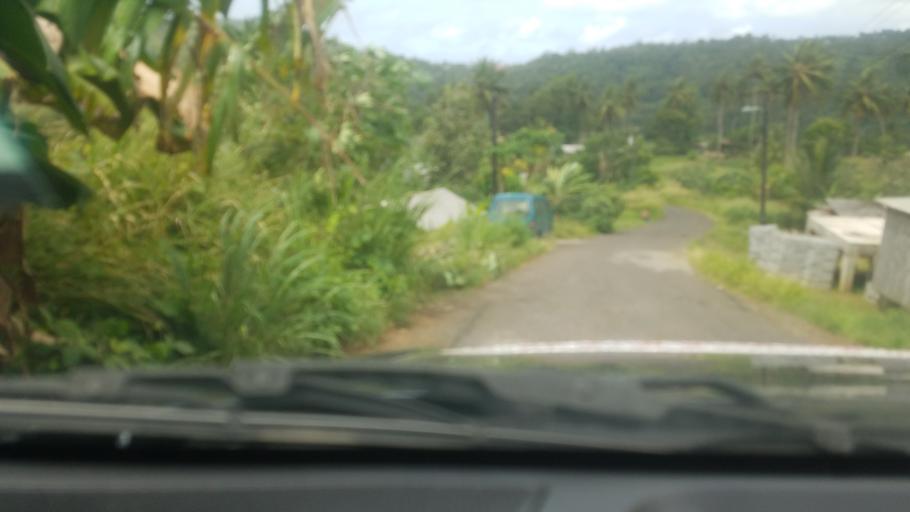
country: LC
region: Micoud Quarter
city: Micoud
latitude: 13.8050
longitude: -60.9492
